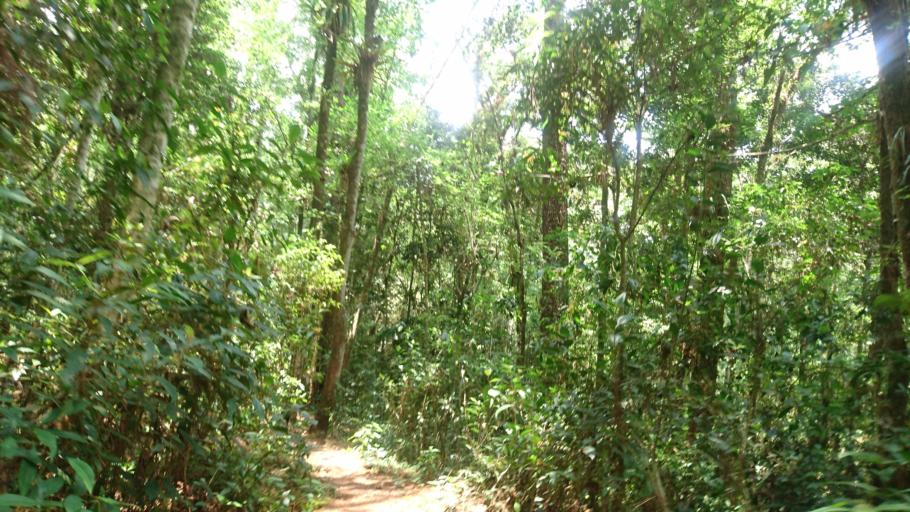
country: GT
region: Huehuetenango
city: Union
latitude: 16.1317
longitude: -91.7290
